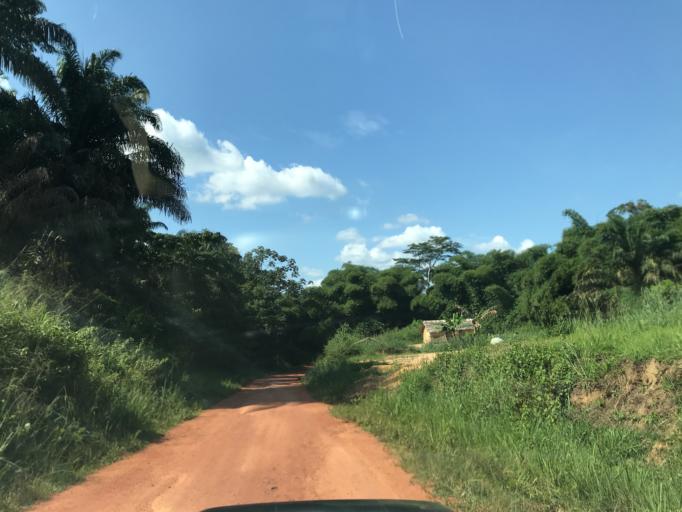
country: CD
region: Eastern Province
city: Kisangani
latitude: 1.2041
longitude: 25.2585
